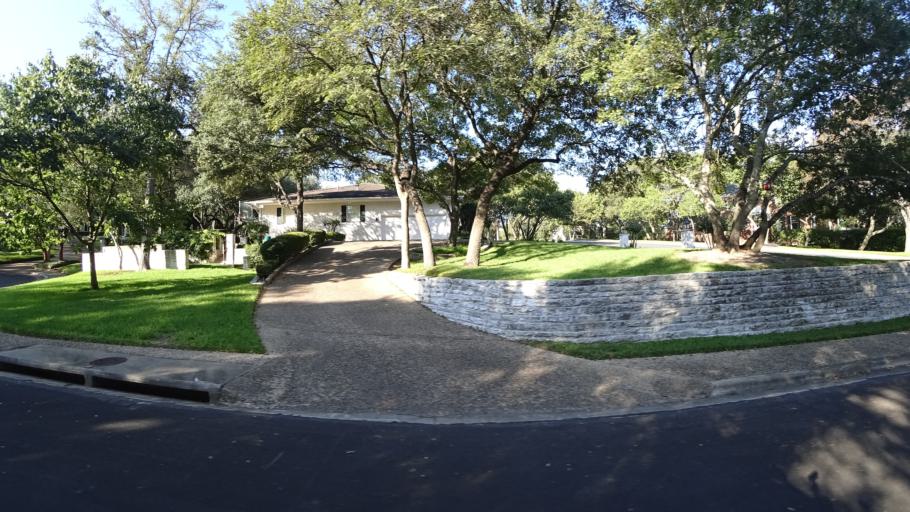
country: US
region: Texas
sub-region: Travis County
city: Rollingwood
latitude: 30.2657
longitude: -97.7959
